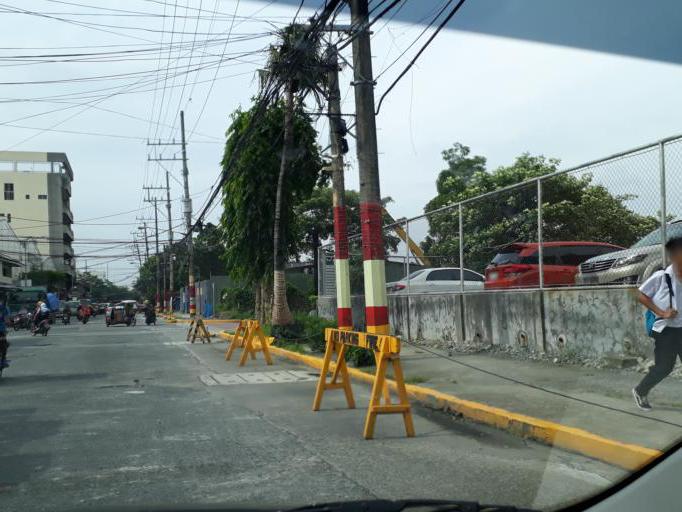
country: PH
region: Metro Manila
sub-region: City of Manila
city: Manila
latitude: 14.6201
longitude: 120.9849
